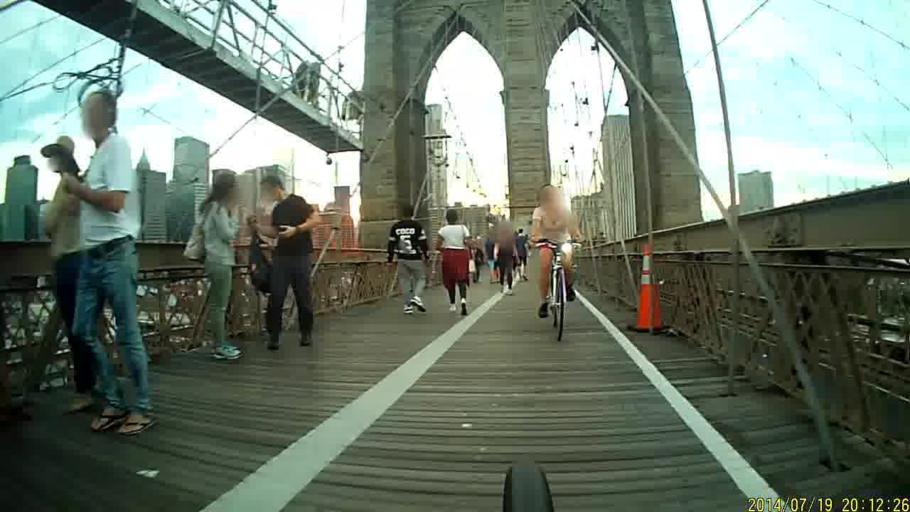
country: US
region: New York
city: New York City
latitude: 40.7068
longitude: -73.9978
